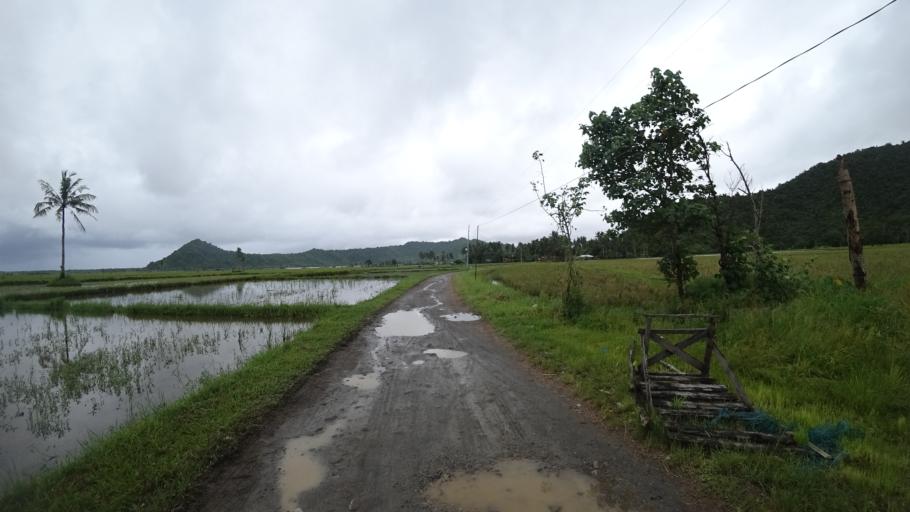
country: PH
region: Eastern Visayas
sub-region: Province of Leyte
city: Bugho
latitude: 10.8013
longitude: 124.9709
